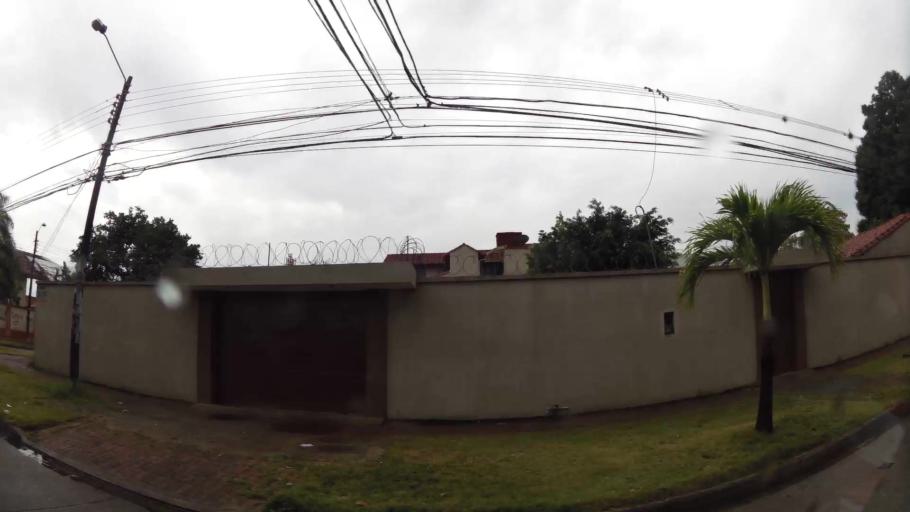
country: BO
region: Santa Cruz
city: Santa Cruz de la Sierra
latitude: -17.8057
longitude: -63.1849
